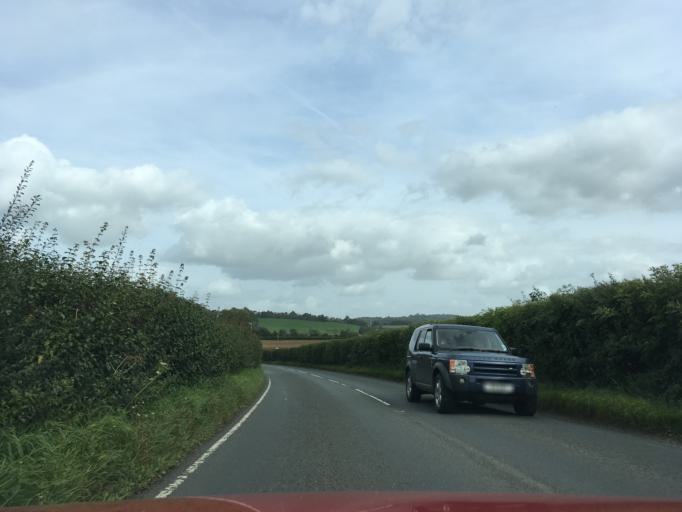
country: GB
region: England
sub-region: South Gloucestershire
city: Charfield
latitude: 51.6312
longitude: -2.3829
